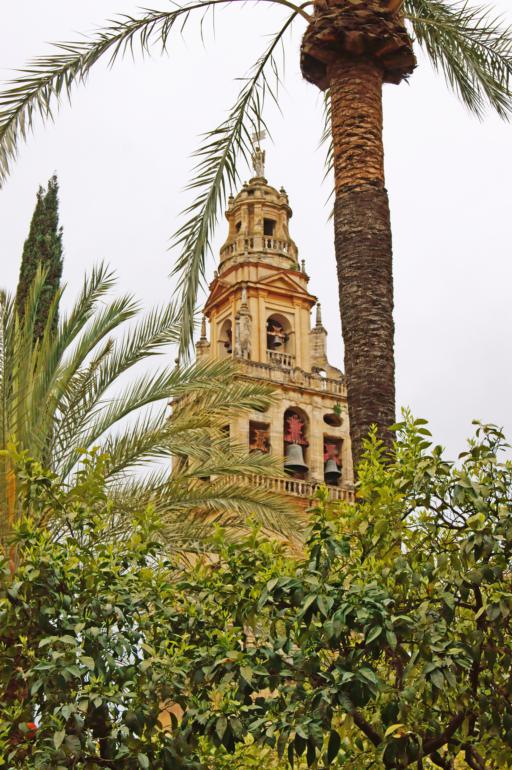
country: ES
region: Andalusia
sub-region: Province of Cordoba
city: Cordoba
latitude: 37.8797
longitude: -4.7793
